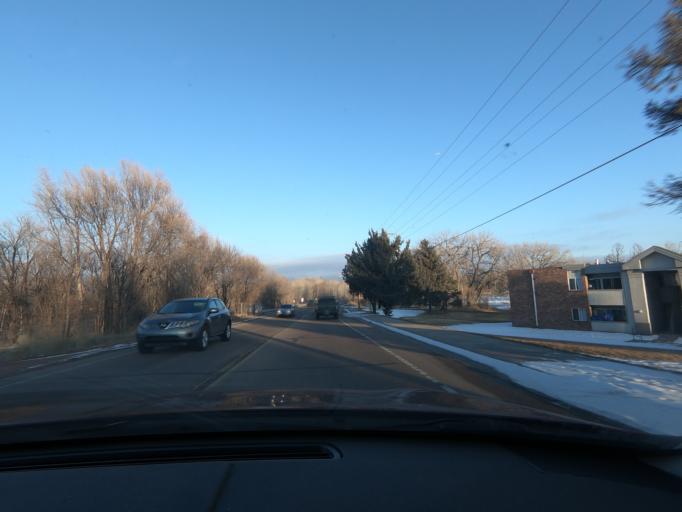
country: US
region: Colorado
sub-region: El Paso County
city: Security-Widefield
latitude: 38.7373
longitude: -104.7130
